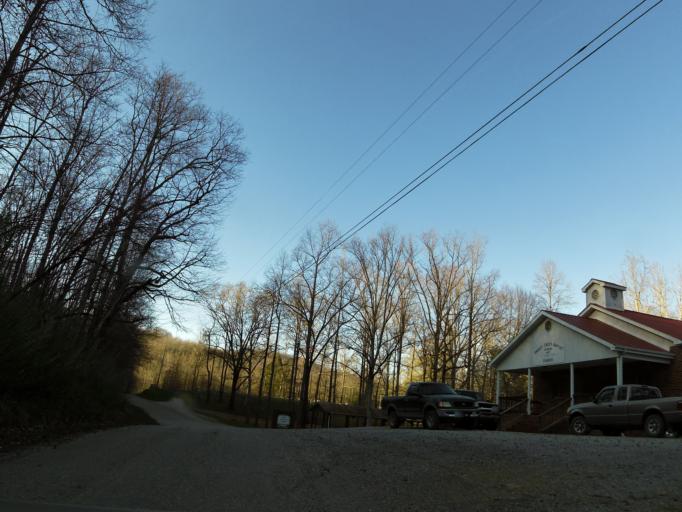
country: US
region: Tennessee
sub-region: Campbell County
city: Caryville
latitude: 36.2541
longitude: -84.3953
